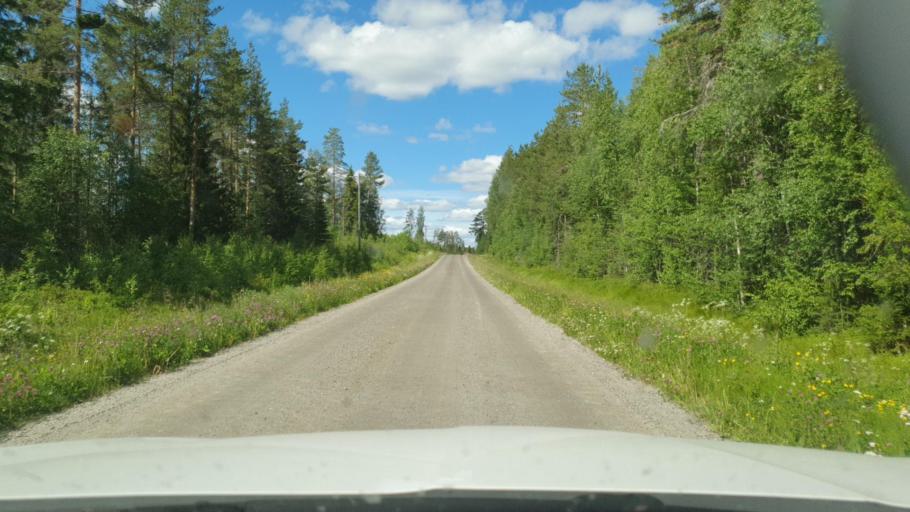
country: SE
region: Vaesterbotten
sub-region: Skelleftea Kommun
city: Backa
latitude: 65.1763
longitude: 21.0880
